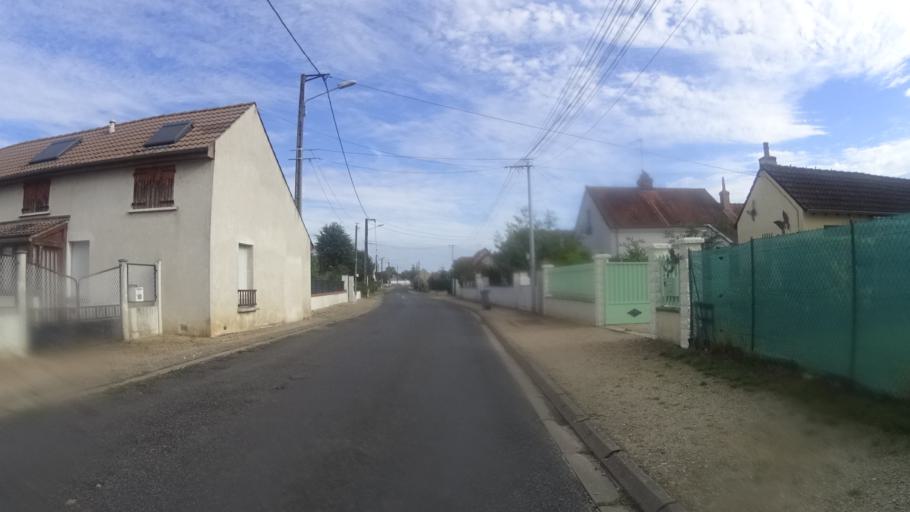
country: FR
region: Centre
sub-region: Departement du Loiret
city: Chateauneuf-sur-Loire
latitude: 47.8732
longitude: 2.2168
